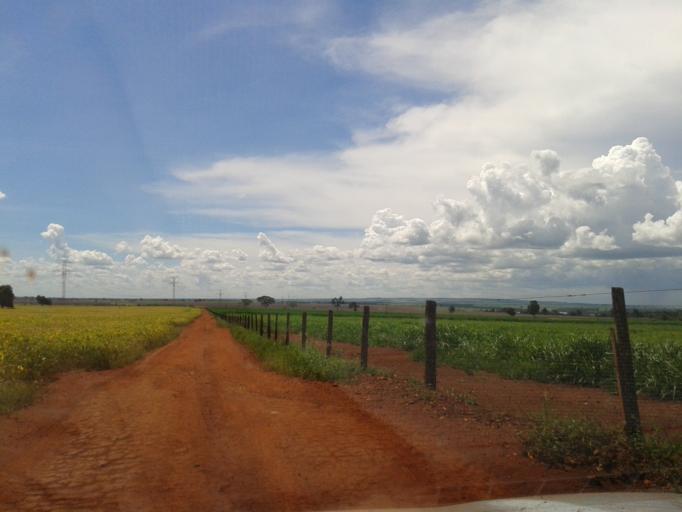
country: BR
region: Minas Gerais
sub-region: Capinopolis
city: Capinopolis
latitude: -18.7011
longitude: -49.7848
